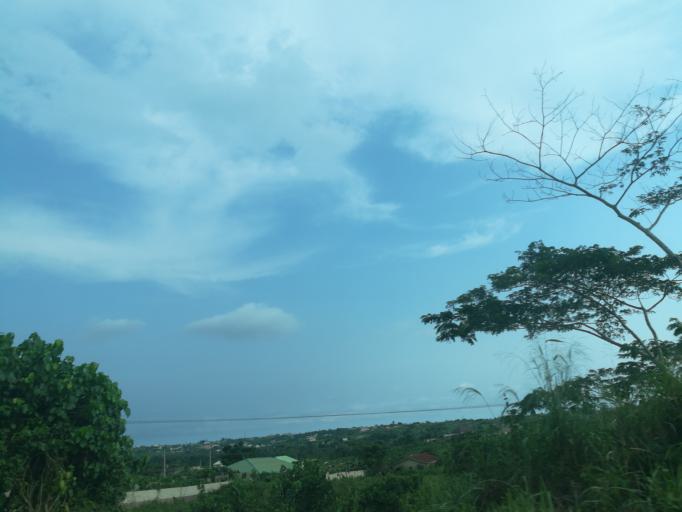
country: NG
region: Lagos
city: Ikorodu
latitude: 6.6193
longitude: 3.6544
